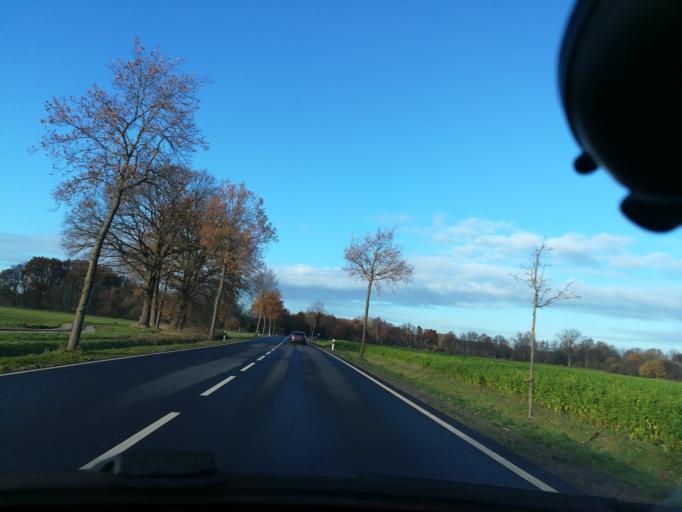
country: DE
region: Lower Saxony
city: Raddestorf
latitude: 52.4282
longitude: 8.9445
